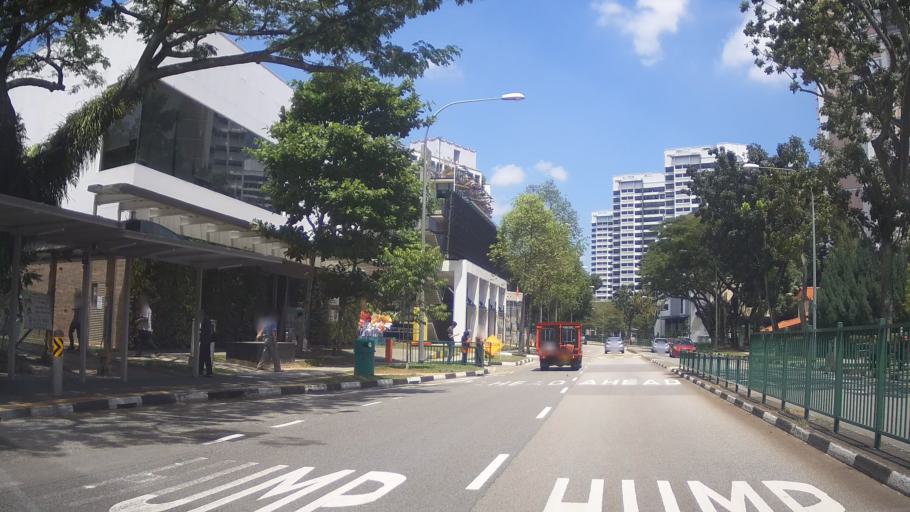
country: SG
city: Singapore
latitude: 1.3347
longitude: 103.7226
